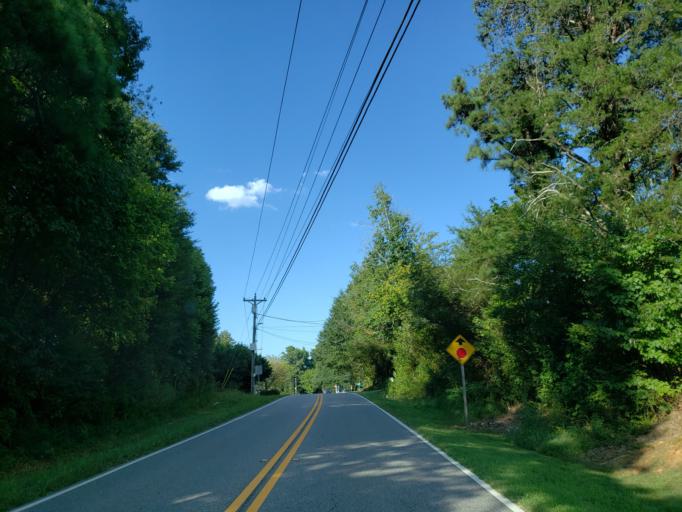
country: US
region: Georgia
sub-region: Forsyth County
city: Cumming
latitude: 34.2426
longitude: -84.1724
